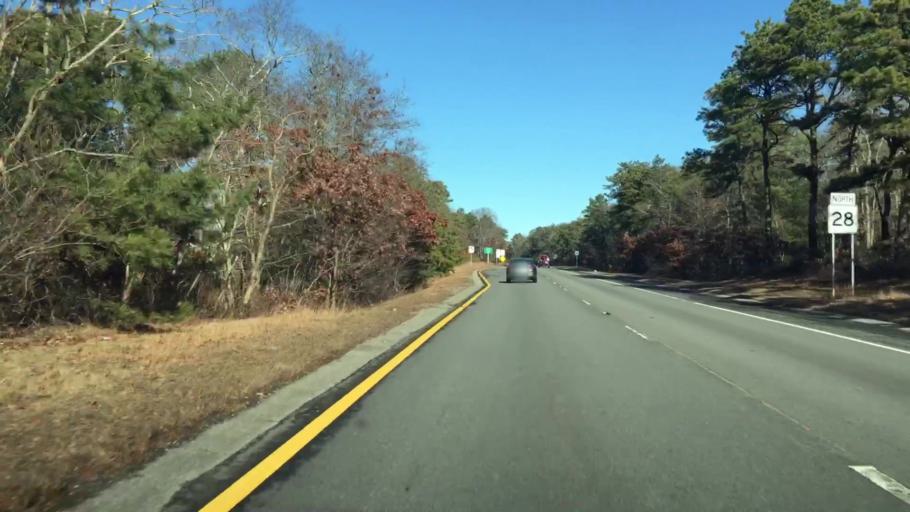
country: US
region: Massachusetts
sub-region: Barnstable County
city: Pocasset
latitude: 41.6961
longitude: -70.5861
